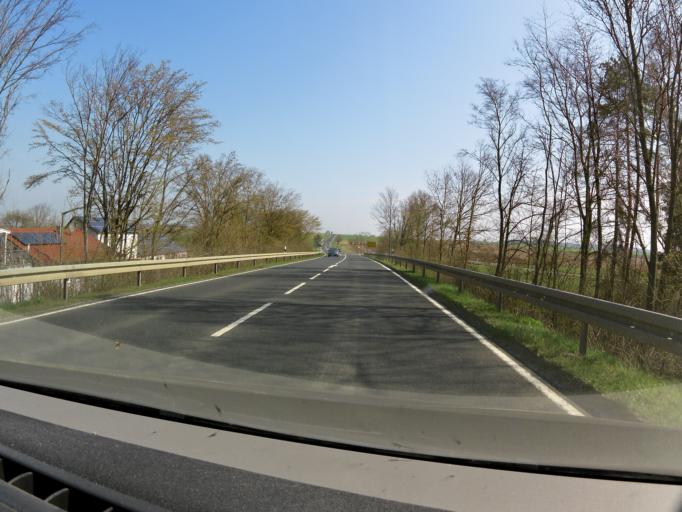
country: DE
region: Bavaria
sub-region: Regierungsbezirk Unterfranken
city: Oberpleichfeld
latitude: 49.8557
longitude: 10.1029
